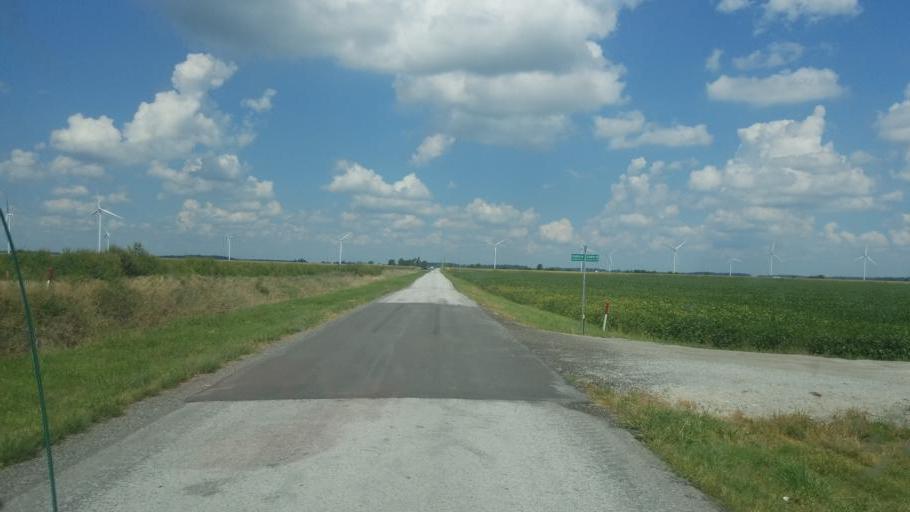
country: US
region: Ohio
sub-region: Hardin County
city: Ada
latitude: 40.7718
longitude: -83.7286
